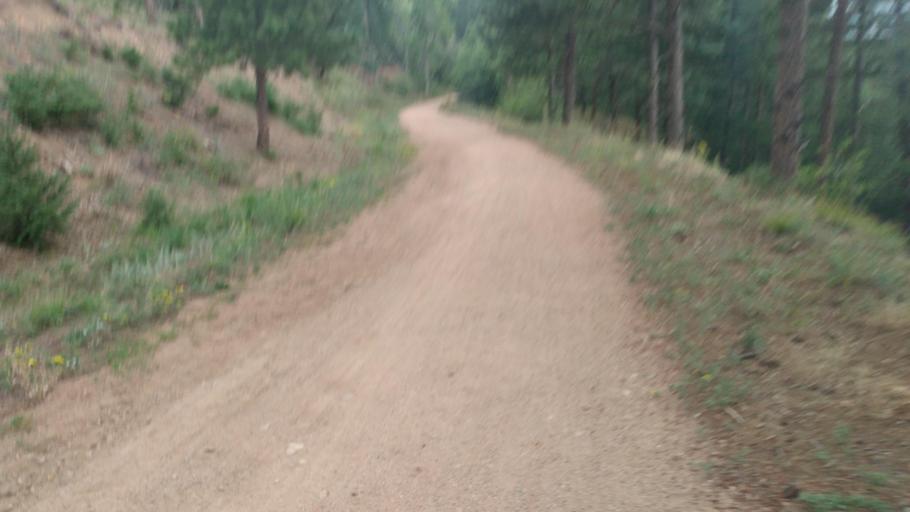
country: US
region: Colorado
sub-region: Boulder County
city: Boulder
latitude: 39.9974
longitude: -105.3101
